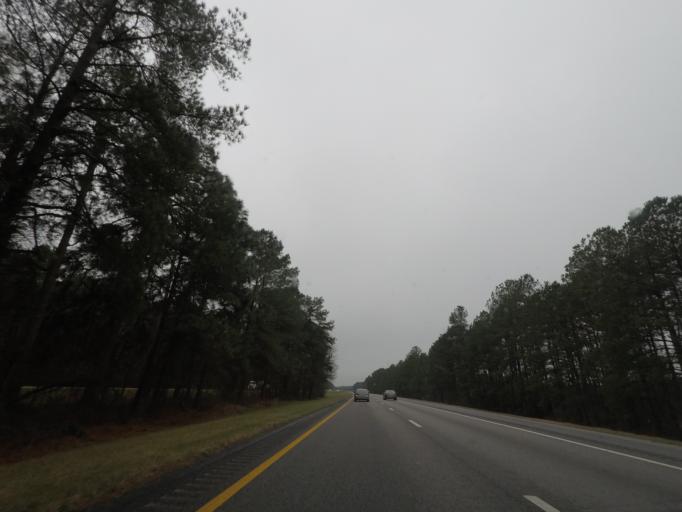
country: US
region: South Carolina
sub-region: Sumter County
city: East Sumter
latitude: 33.9098
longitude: -80.0883
